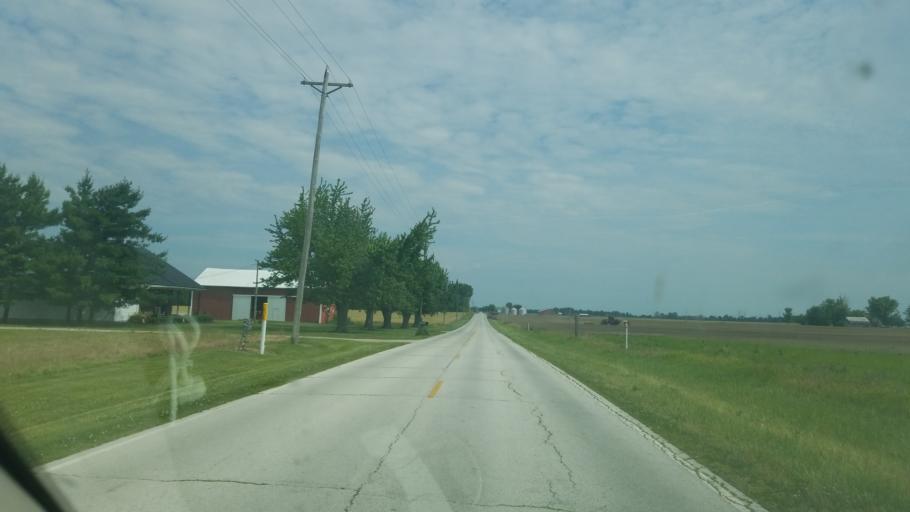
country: US
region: Ohio
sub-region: Seneca County
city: Fostoria
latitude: 41.1034
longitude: -83.4785
